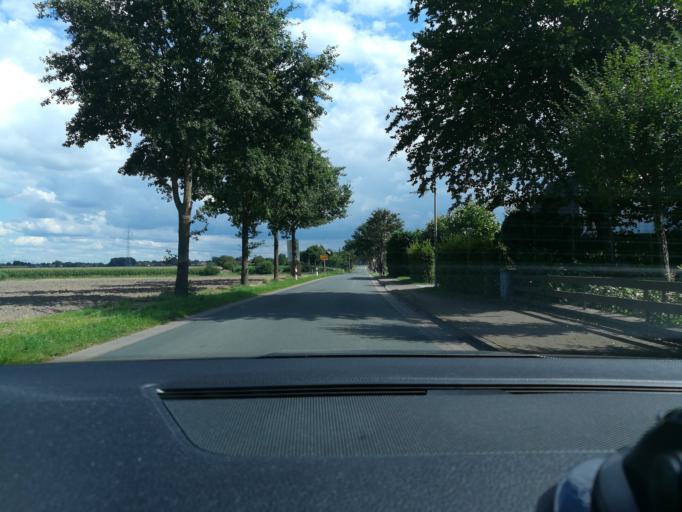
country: DE
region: North Rhine-Westphalia
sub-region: Regierungsbezirk Detmold
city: Hille
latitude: 52.3376
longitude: 8.8094
